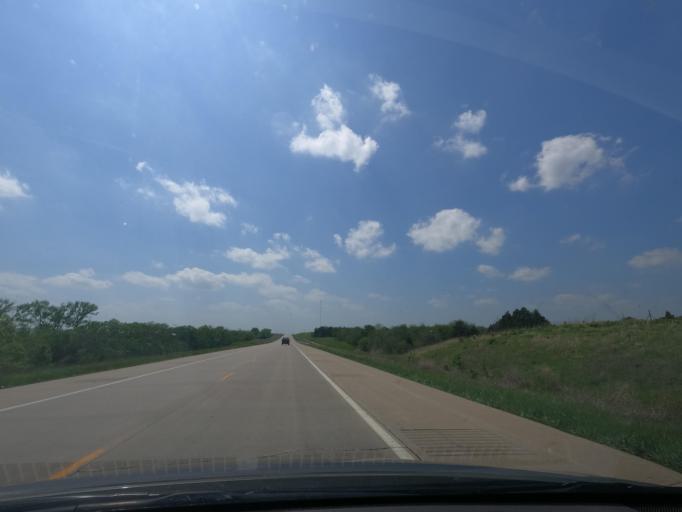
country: US
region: Kansas
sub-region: Elk County
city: Howard
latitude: 37.6276
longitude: -96.0877
